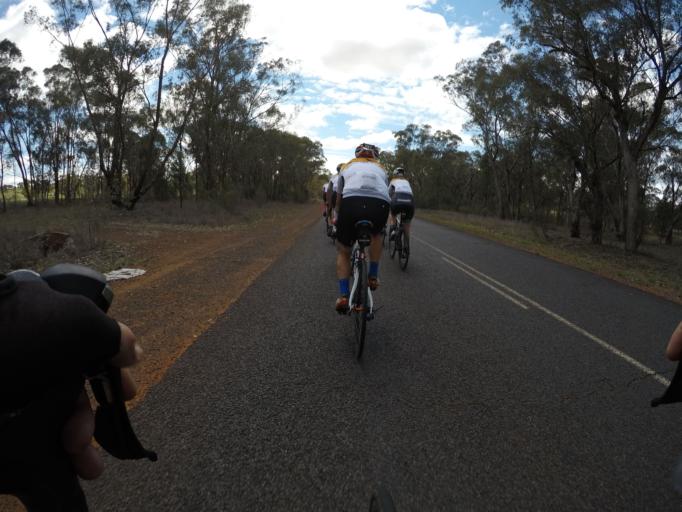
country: AU
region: New South Wales
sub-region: Dubbo Municipality
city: Dubbo
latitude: -32.3850
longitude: 148.5732
